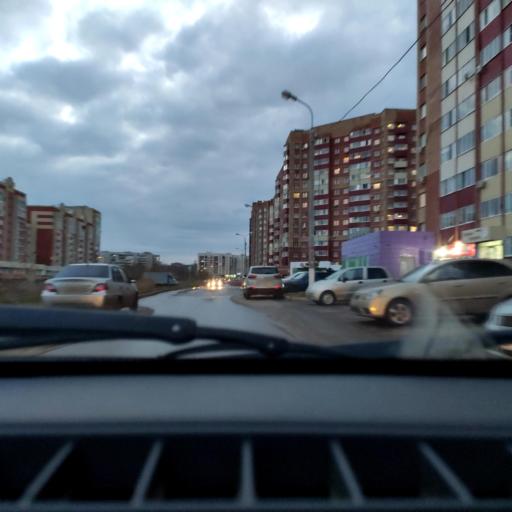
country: RU
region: Bashkortostan
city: Mikhaylovka
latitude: 54.7134
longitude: 55.8437
